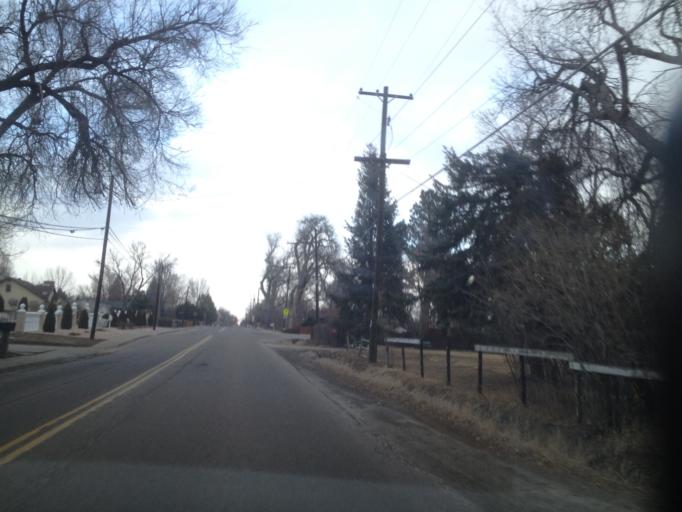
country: US
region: Colorado
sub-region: Adams County
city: Berkley
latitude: 39.8089
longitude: -105.0441
